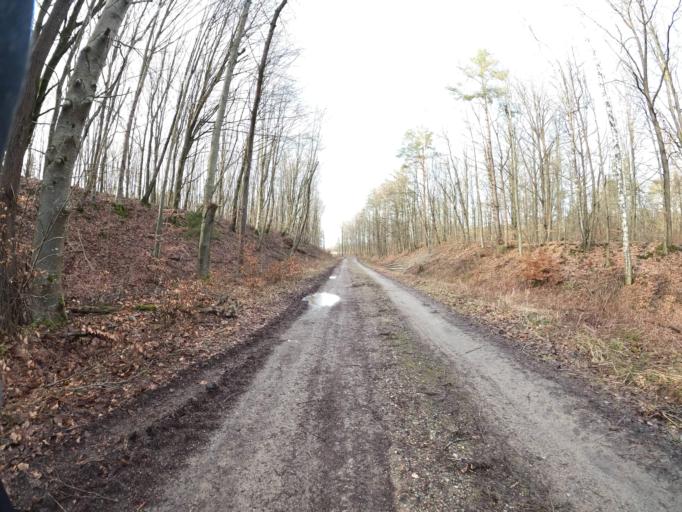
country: PL
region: West Pomeranian Voivodeship
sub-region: Powiat koszalinski
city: Polanow
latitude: 54.1712
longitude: 16.7501
